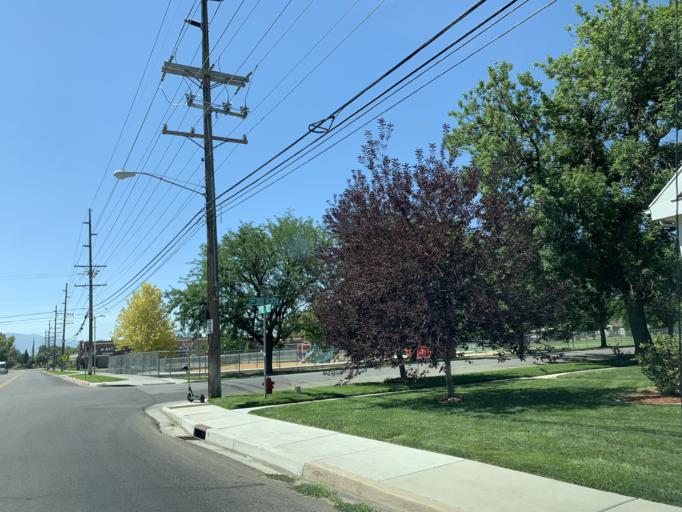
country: US
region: Utah
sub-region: Utah County
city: Provo
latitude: 40.2366
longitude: -111.6466
